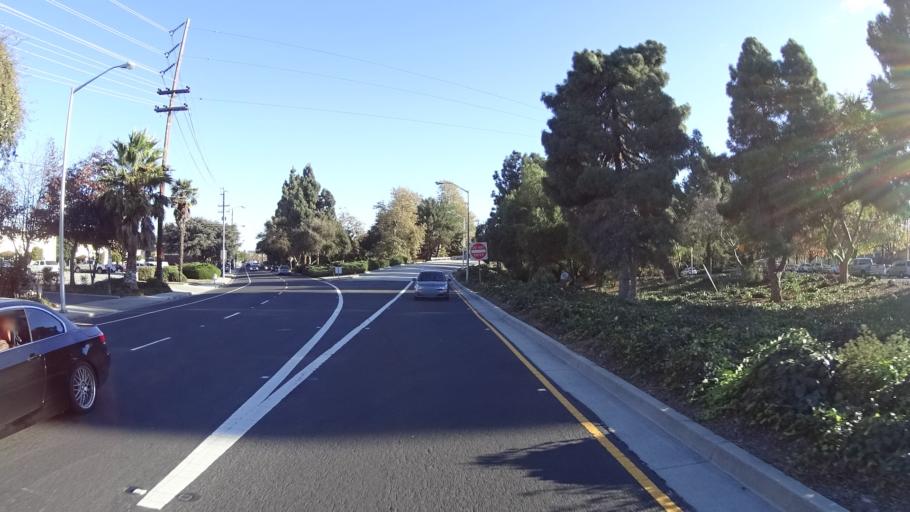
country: US
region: California
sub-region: Santa Clara County
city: Santa Clara
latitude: 37.3596
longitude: -121.9408
